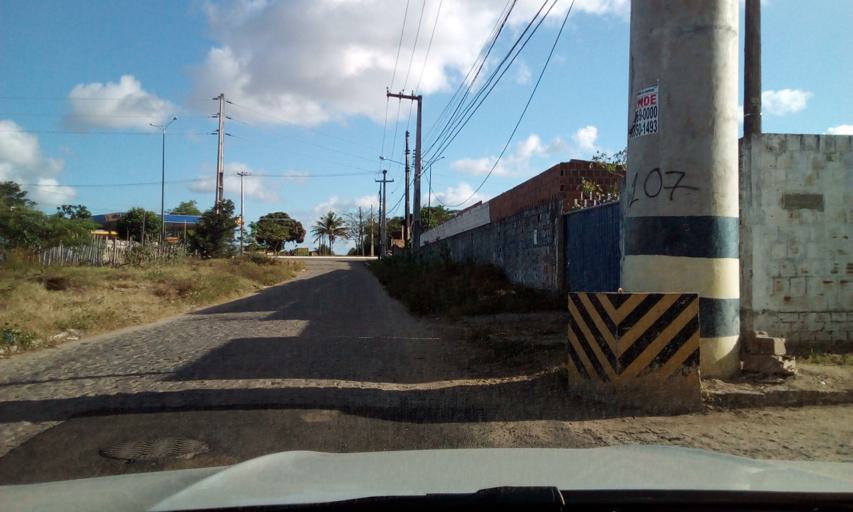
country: BR
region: Paraiba
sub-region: Bayeux
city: Bayeux
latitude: -7.1429
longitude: -34.9066
